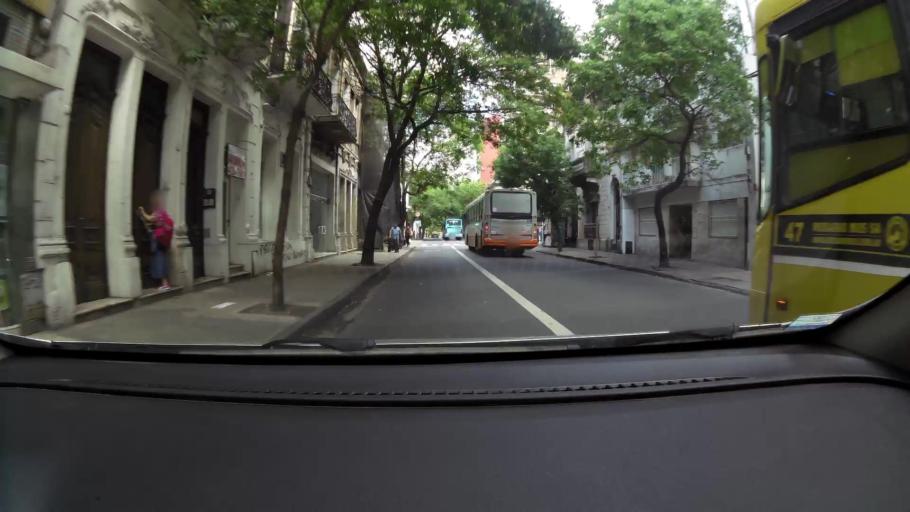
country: AR
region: Santa Fe
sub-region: Departamento de Rosario
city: Rosario
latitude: -32.9434
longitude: -60.6471
